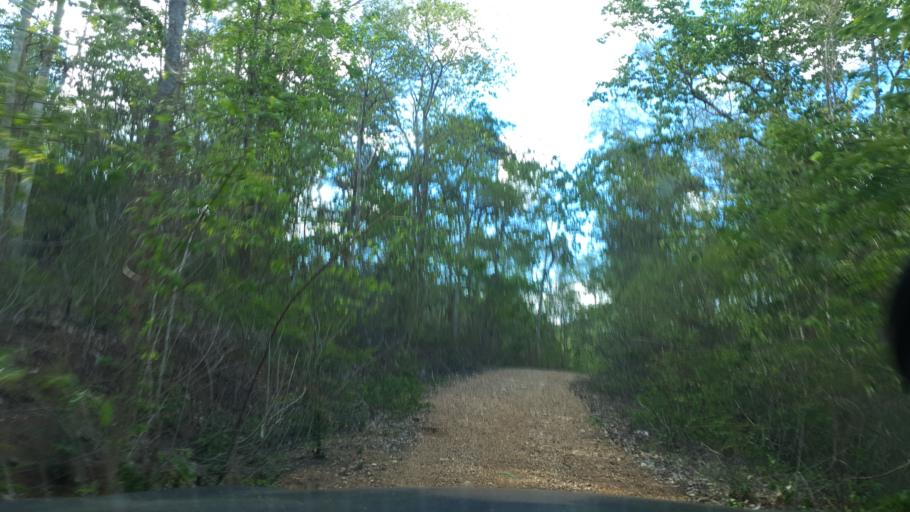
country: TH
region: Lampang
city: Sop Prap
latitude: 17.8452
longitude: 99.2857
